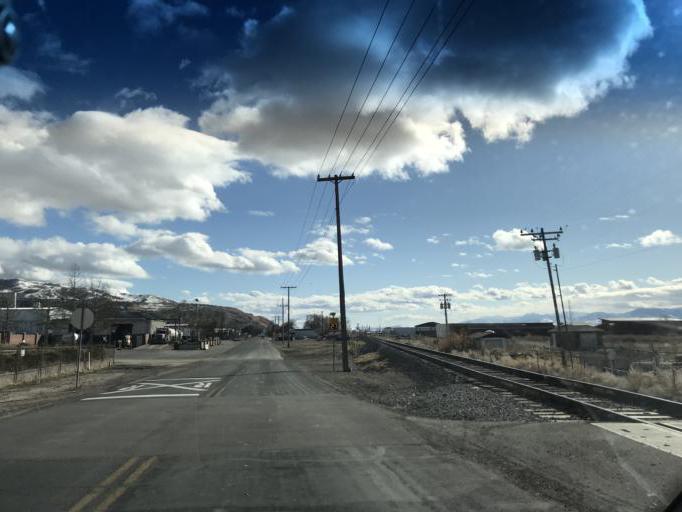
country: US
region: Utah
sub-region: Davis County
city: Woods Cross
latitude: 40.8685
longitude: -111.9119
